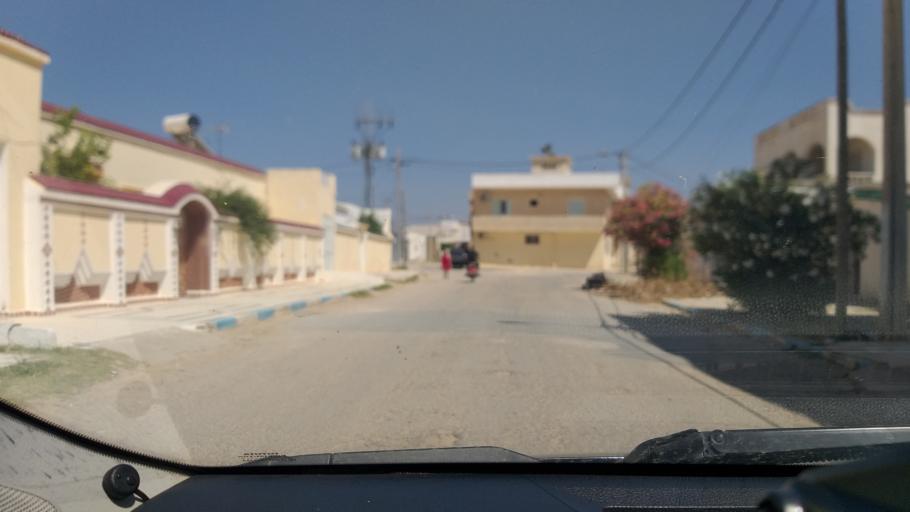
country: TN
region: Al Mahdiyah
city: El Jem
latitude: 35.2922
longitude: 10.7144
